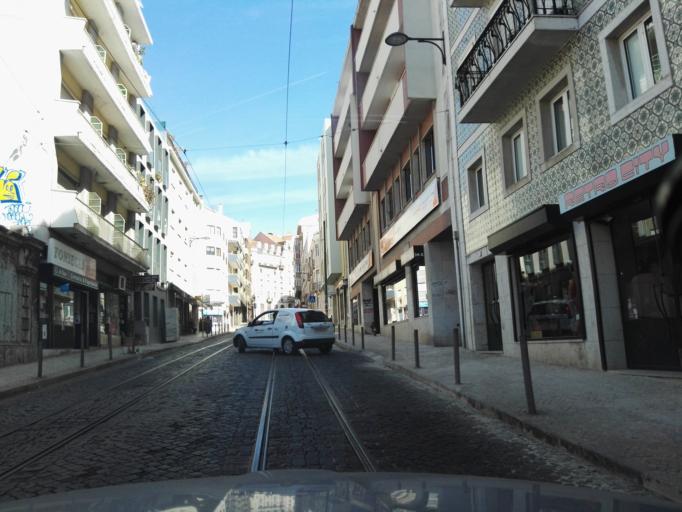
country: PT
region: Lisbon
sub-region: Lisbon
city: Lisbon
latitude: 38.7235
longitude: -9.1349
